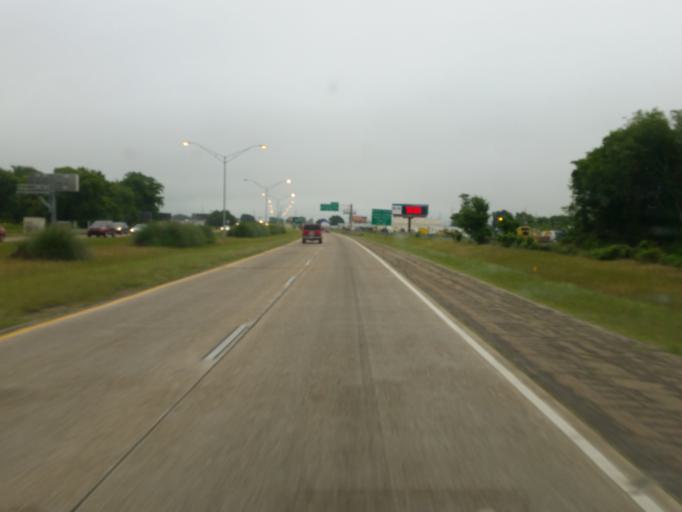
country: US
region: Louisiana
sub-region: Bossier Parish
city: Bossier City
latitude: 32.5264
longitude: -93.6849
